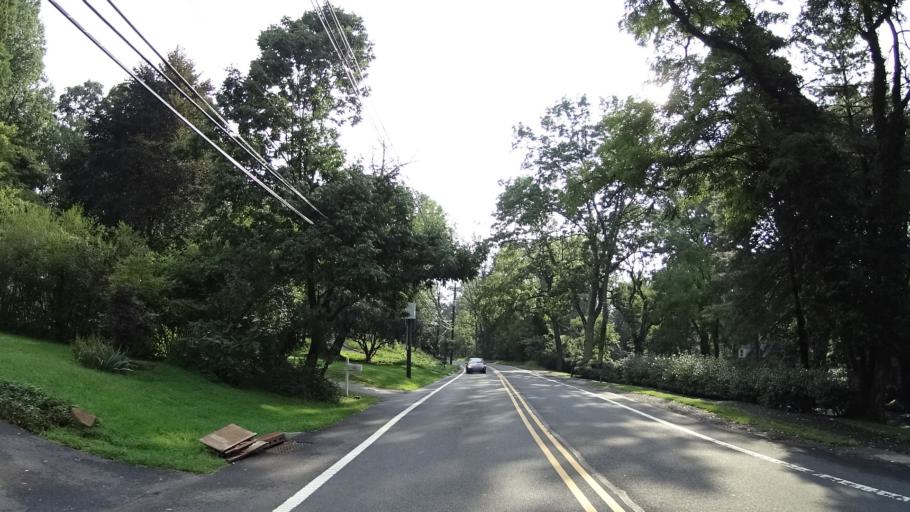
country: US
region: New Jersey
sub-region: Union County
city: New Providence
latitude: 40.7154
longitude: -74.4177
